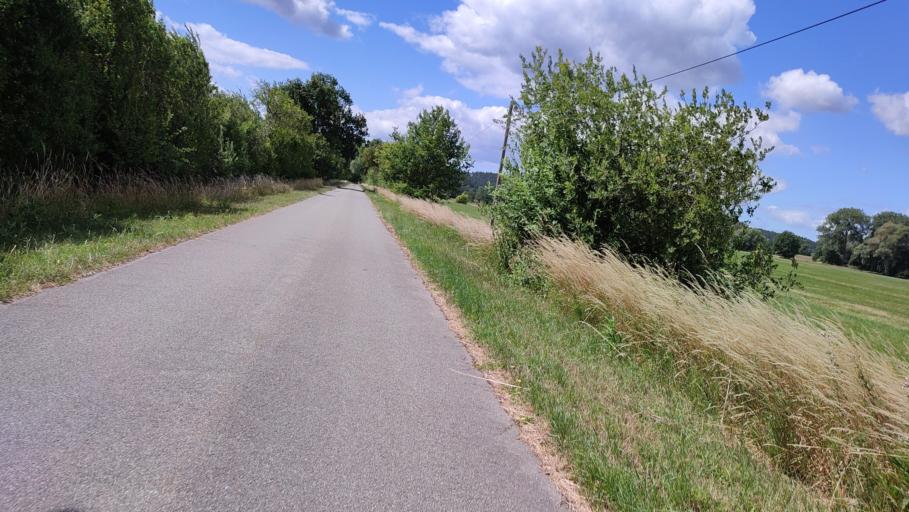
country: DE
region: Lower Saxony
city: Hitzacker
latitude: 53.2006
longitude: 10.9891
